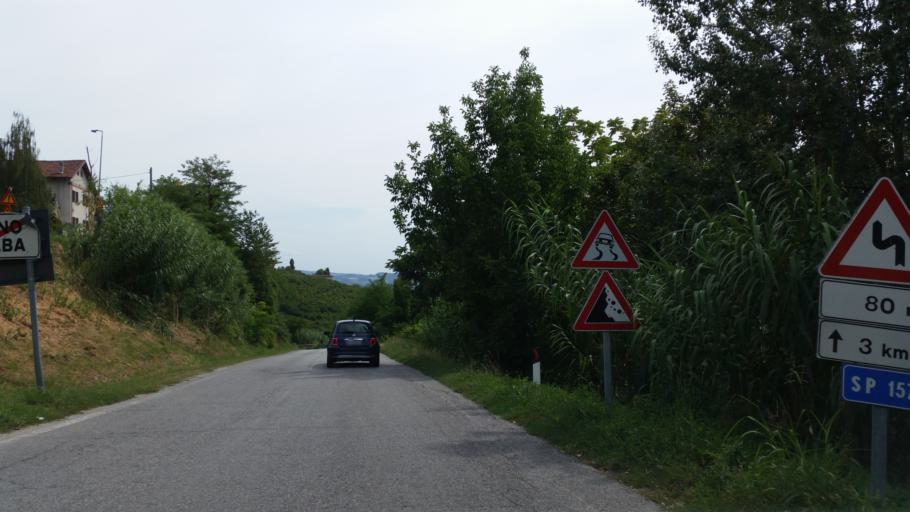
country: IT
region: Piedmont
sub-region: Provincia di Cuneo
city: Diano d'Alba
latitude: 44.6559
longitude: 8.0253
